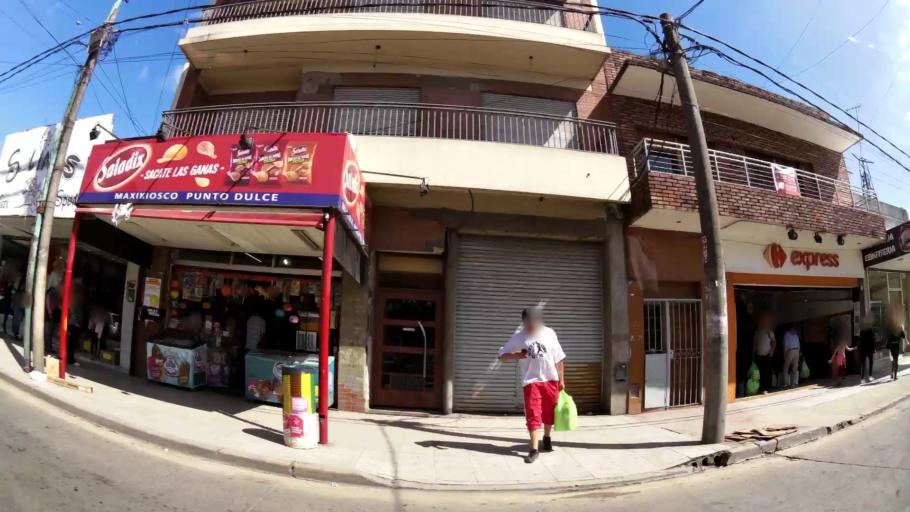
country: AR
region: Buenos Aires
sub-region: Partido de Quilmes
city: Quilmes
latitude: -34.8079
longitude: -58.2754
